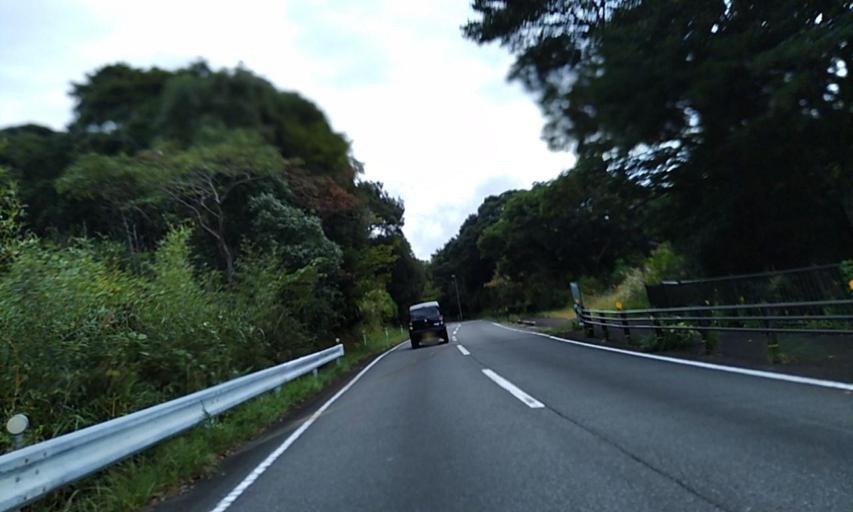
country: JP
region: Wakayama
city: Shingu
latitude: 33.4678
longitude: 135.8262
